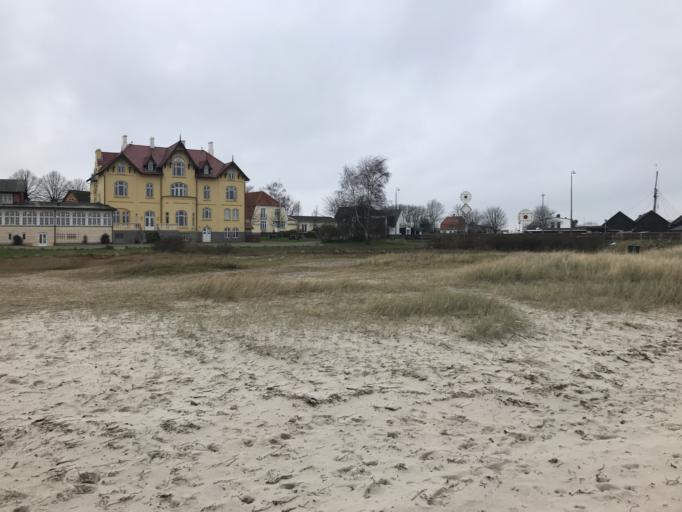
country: DK
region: South Denmark
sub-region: Haderslev Kommune
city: Starup
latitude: 55.2605
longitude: 9.7131
